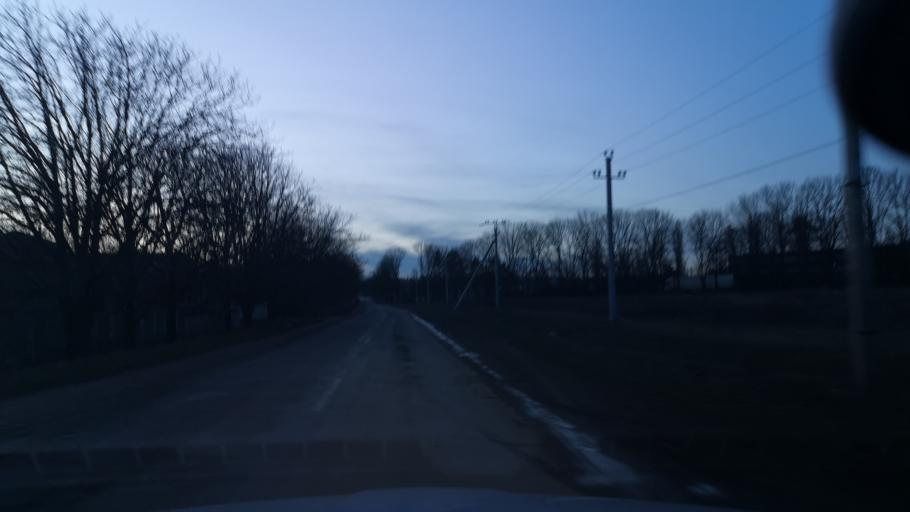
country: MD
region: Orhei
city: Orhei
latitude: 47.2875
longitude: 28.8651
